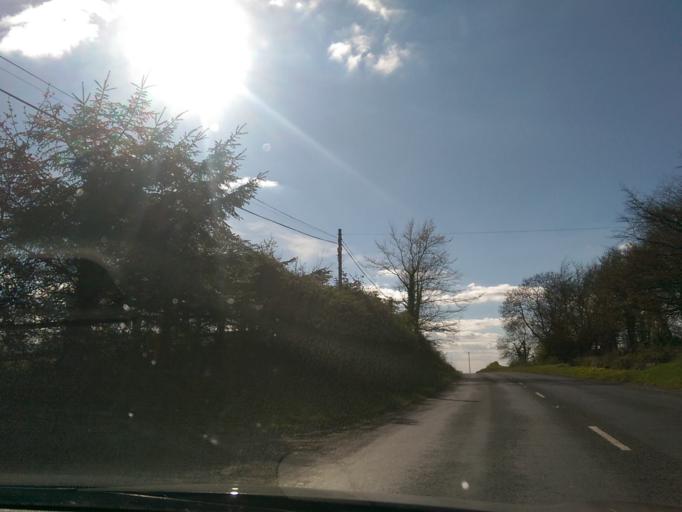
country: IE
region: Leinster
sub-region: Uibh Fhaili
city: Birr
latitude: 53.1017
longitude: -7.9964
